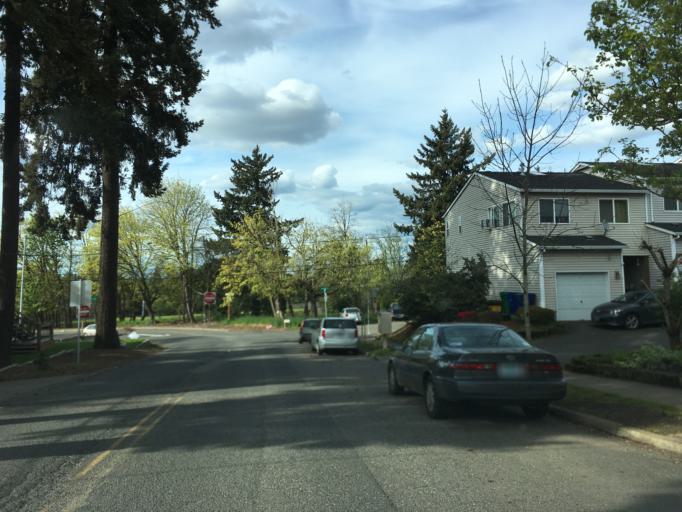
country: US
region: Oregon
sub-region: Multnomah County
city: Lents
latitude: 45.5452
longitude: -122.5565
